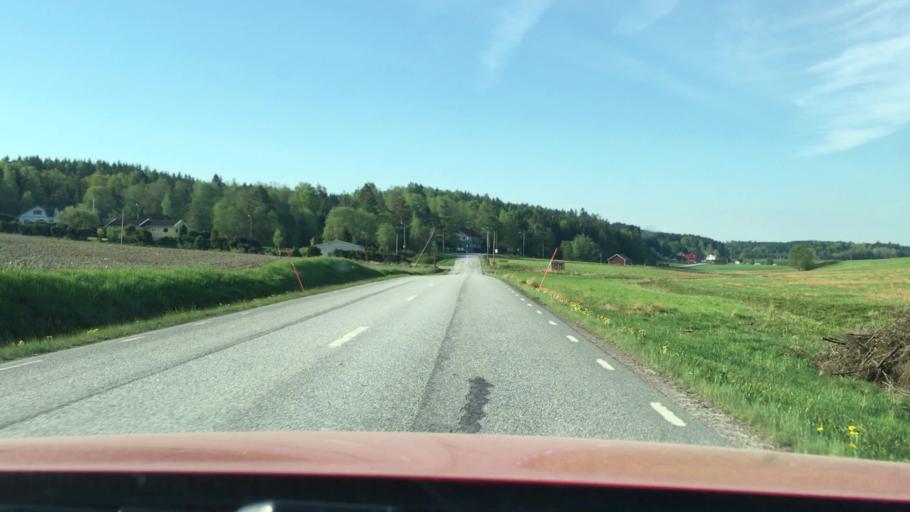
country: SE
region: Vaestra Goetaland
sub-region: Munkedals Kommun
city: Munkedal
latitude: 58.6078
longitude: 11.5589
